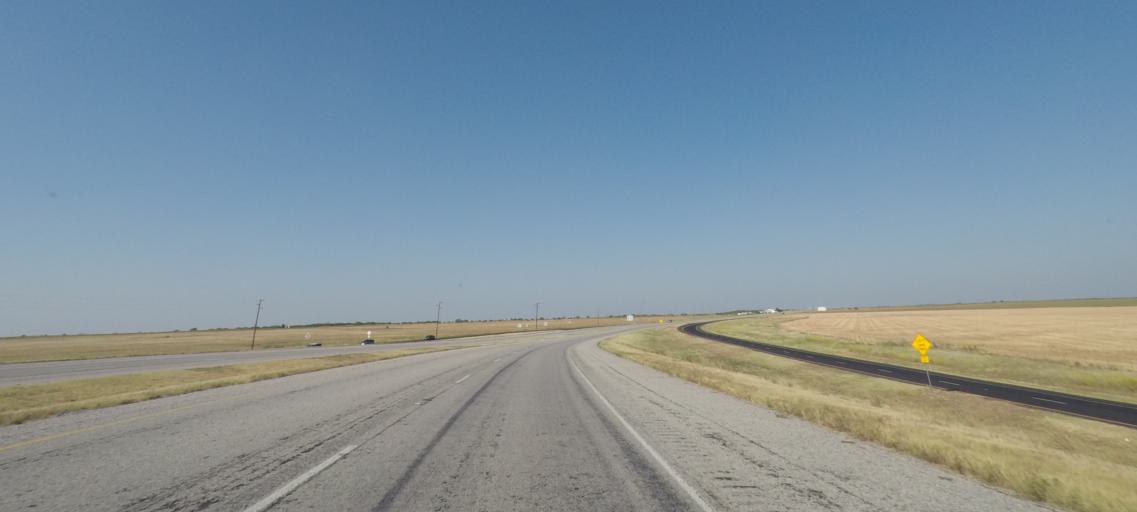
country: US
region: Texas
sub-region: Baylor County
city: Seymour
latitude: 33.6166
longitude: -99.2420
